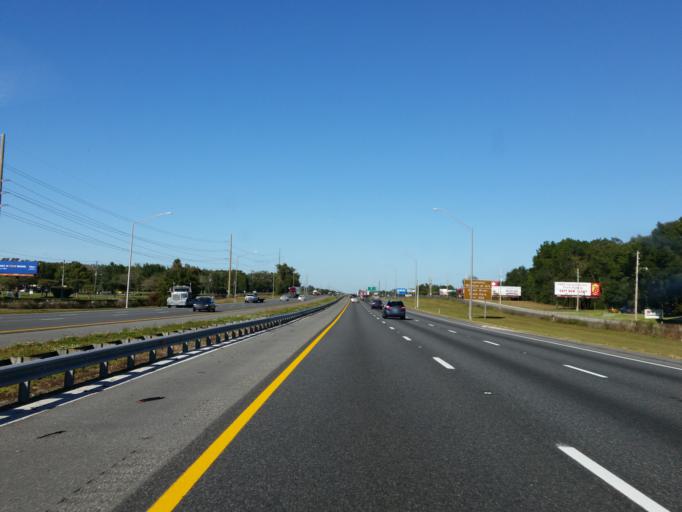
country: US
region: Florida
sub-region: Marion County
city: Ocala
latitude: 29.1754
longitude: -82.1847
